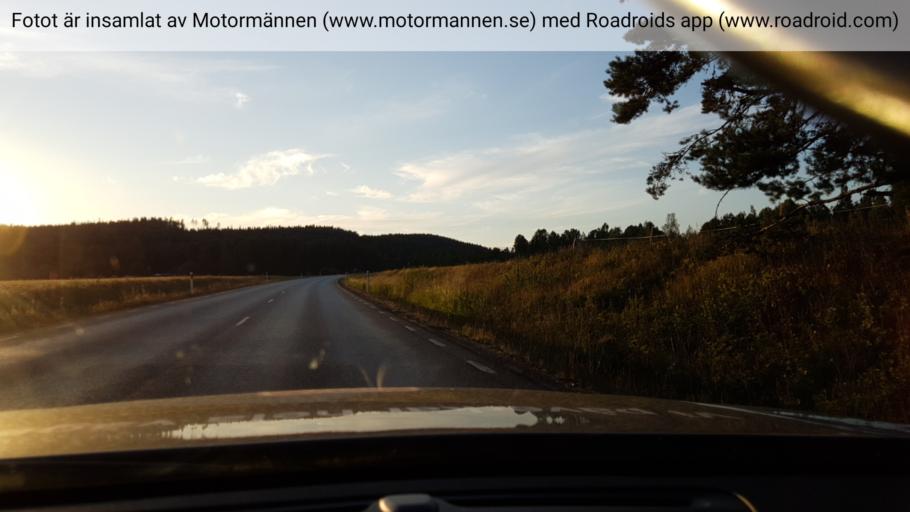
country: SE
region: Vaermland
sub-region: Storfors Kommun
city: Storfors
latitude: 59.5069
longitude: 14.3100
